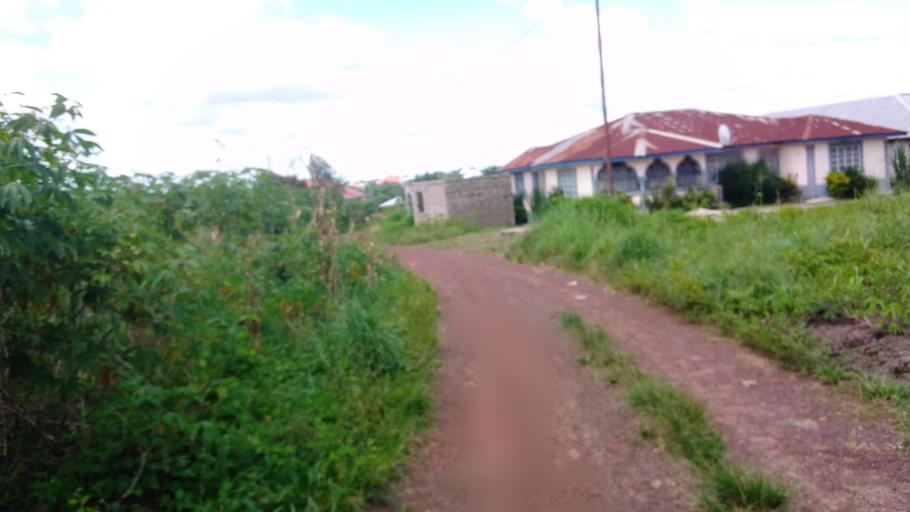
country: SL
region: Northern Province
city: Makeni
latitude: 8.8817
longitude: -12.0260
